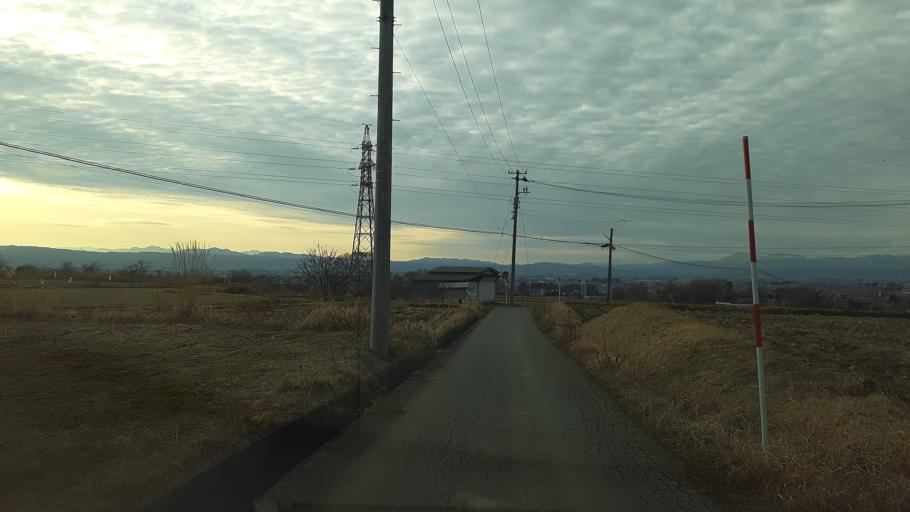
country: JP
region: Fukushima
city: Kitakata
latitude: 37.5255
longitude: 139.9530
